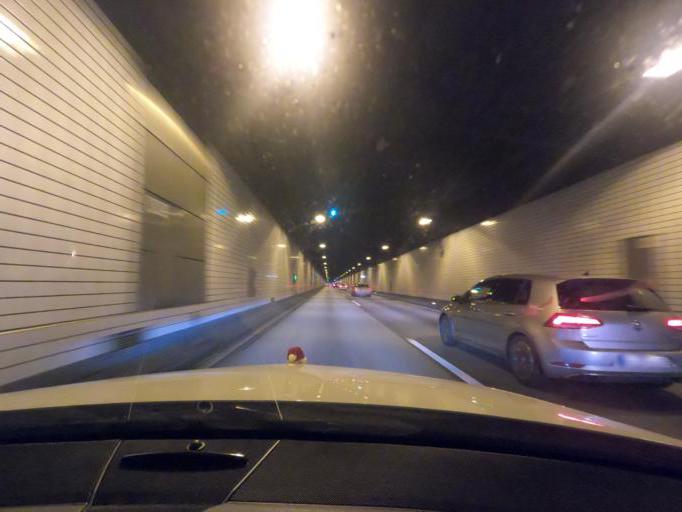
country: DE
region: Hamburg
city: Altona
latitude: 53.5513
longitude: 9.9319
